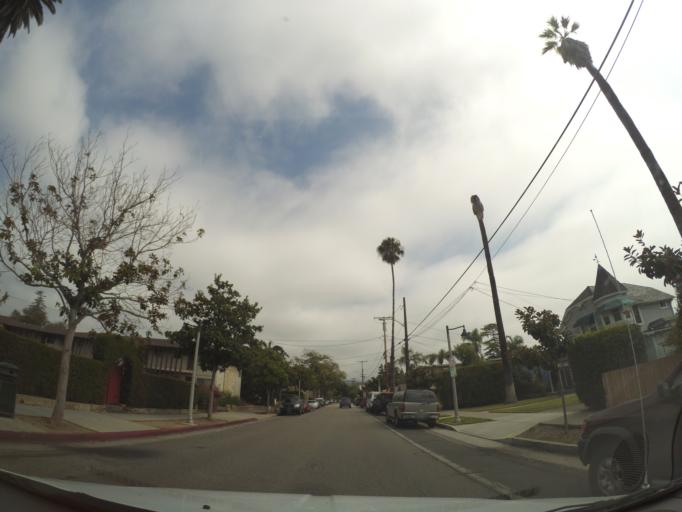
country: US
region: California
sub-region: Santa Barbara County
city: Santa Barbara
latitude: 34.4202
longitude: -119.7076
